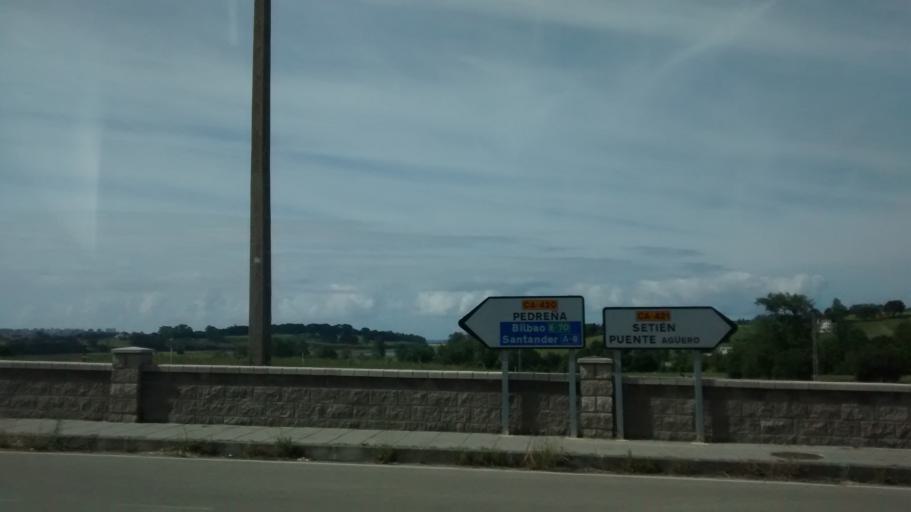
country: ES
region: Cantabria
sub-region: Provincia de Cantabria
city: Santander
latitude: 43.4214
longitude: -3.7501
